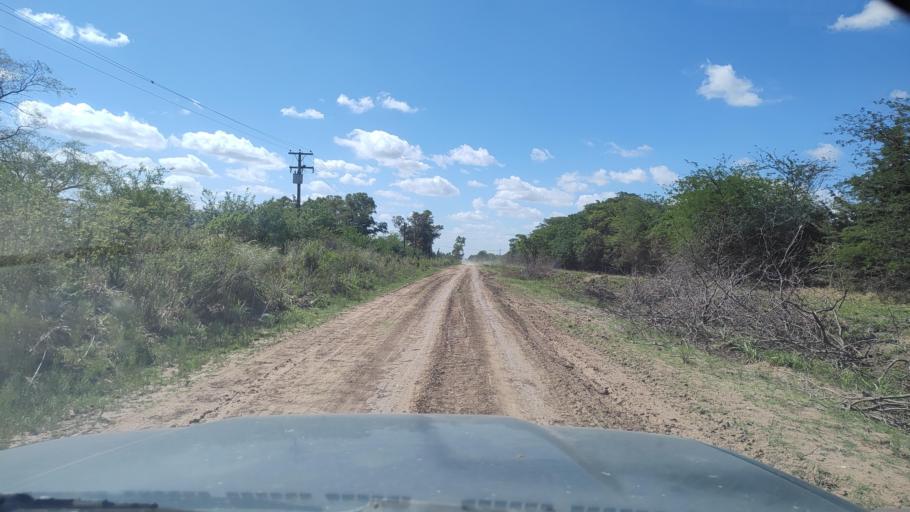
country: AR
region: Buenos Aires
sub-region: Partido de Lujan
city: Lujan
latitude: -34.5342
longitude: -59.1482
